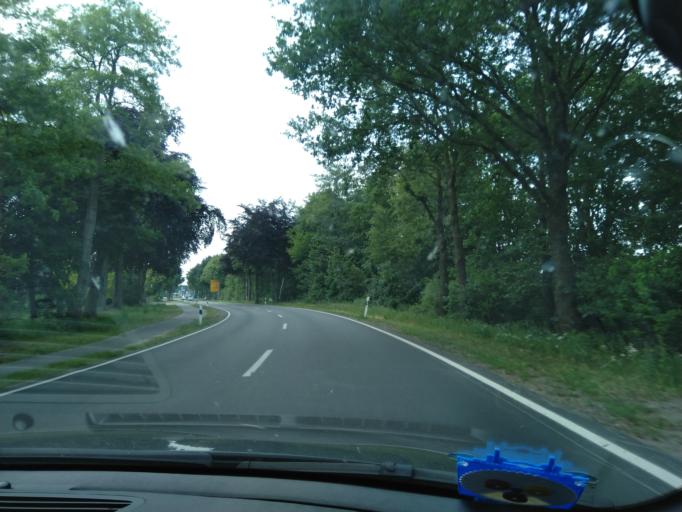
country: NL
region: Drenthe
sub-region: Gemeente Coevorden
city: Coevorden
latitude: 52.6448
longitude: 6.7575
